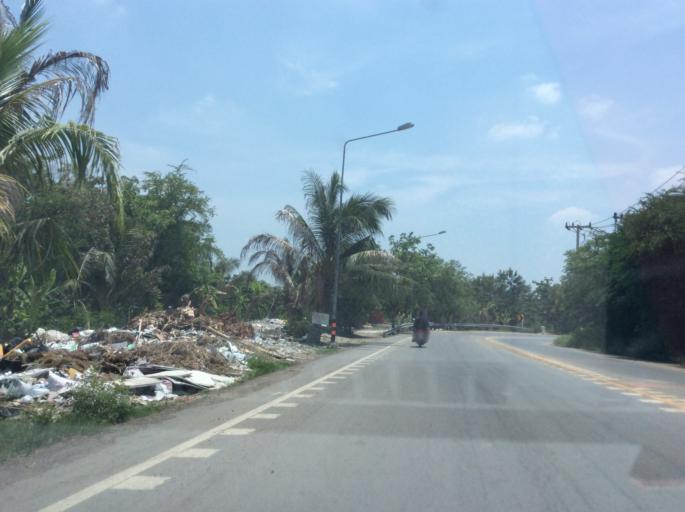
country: TH
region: Pathum Thani
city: Ban Rangsit
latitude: 14.0191
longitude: 100.7793
